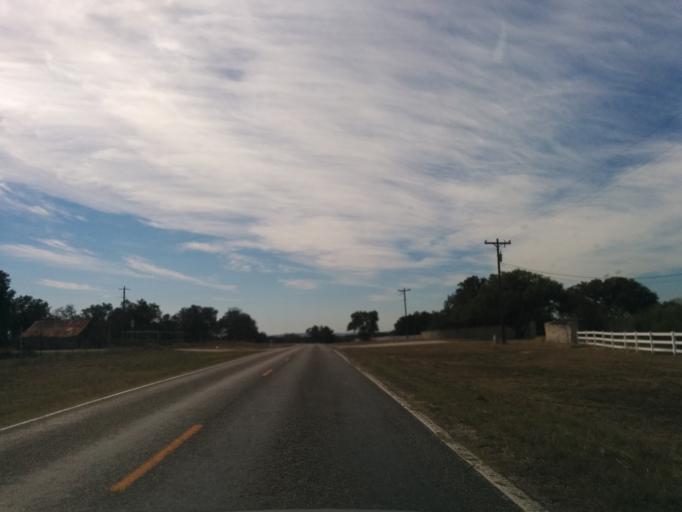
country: US
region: Texas
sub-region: Bexar County
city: Fair Oaks Ranch
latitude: 29.9301
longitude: -98.5700
